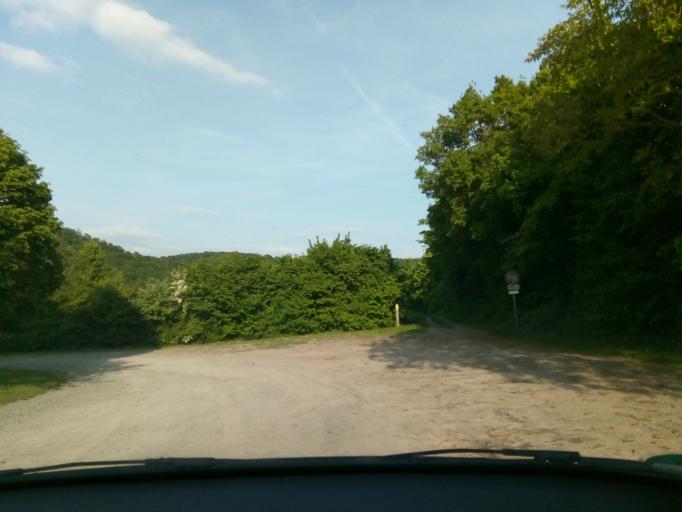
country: DE
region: Bavaria
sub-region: Regierungsbezirk Unterfranken
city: Oberschwarzach
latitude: 49.8716
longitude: 10.4350
